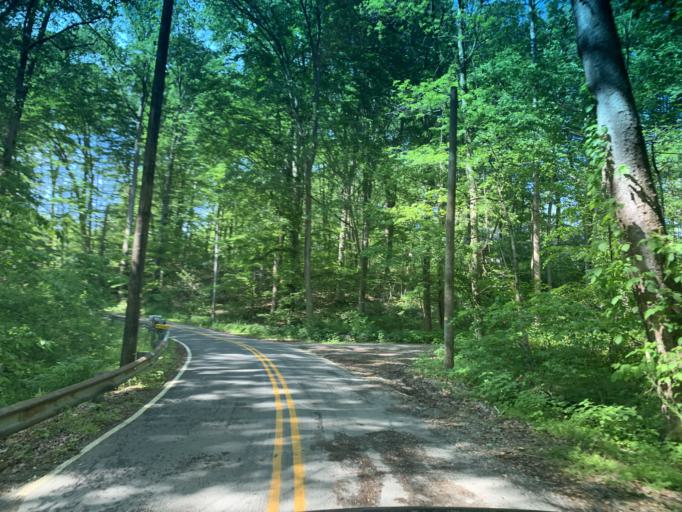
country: US
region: Maryland
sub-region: Cecil County
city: Rising Sun
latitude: 39.6904
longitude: -76.1860
